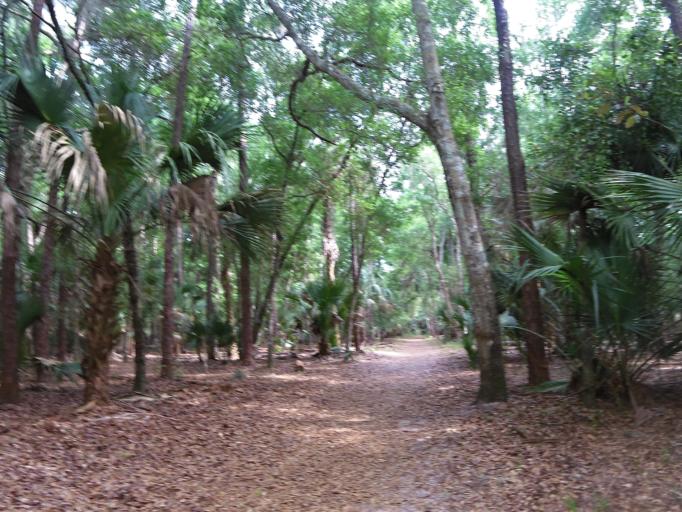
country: US
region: Florida
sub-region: Volusia County
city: Ormond-by-the-Sea
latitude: 29.3907
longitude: -81.1324
